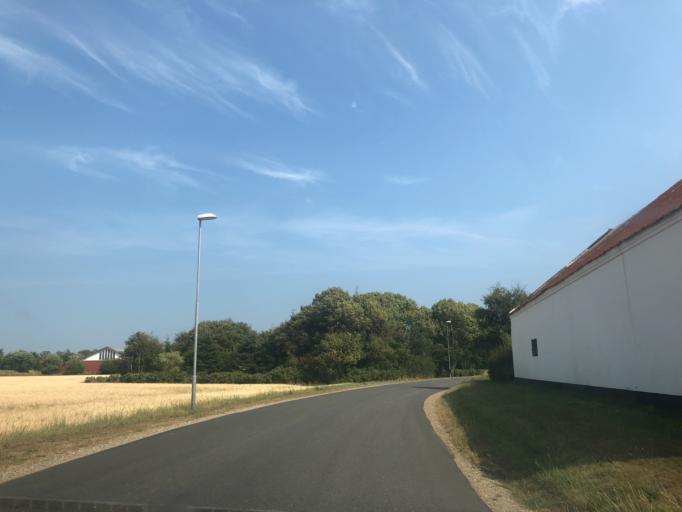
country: DK
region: North Denmark
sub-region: Morso Kommune
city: Nykobing Mors
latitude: 56.8206
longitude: 9.0029
